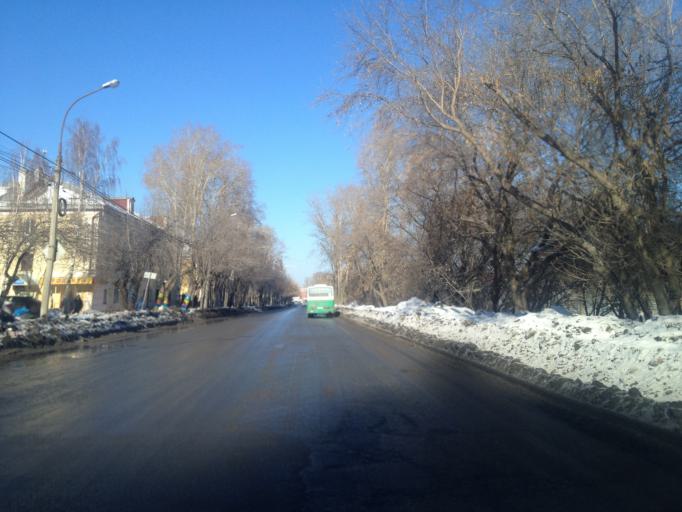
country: RU
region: Sverdlovsk
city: Sovkhoznyy
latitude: 56.7645
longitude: 60.6133
